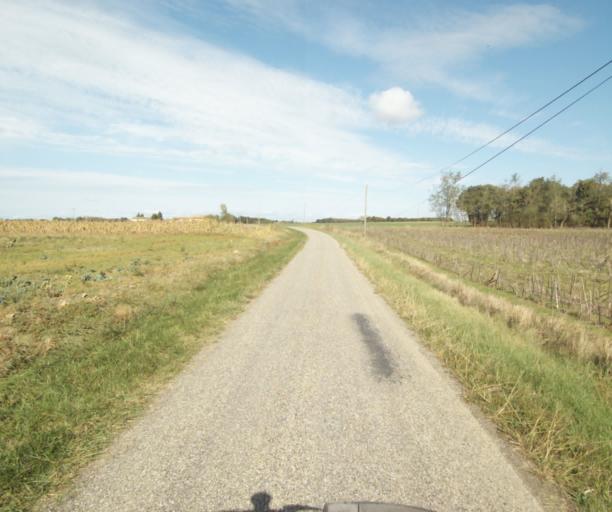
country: FR
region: Midi-Pyrenees
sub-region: Departement du Tarn-et-Garonne
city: Verdun-sur-Garonne
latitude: 43.8434
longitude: 1.1790
